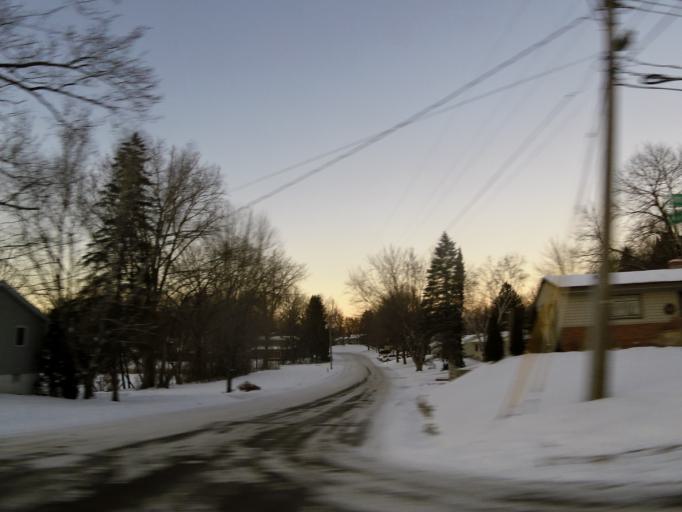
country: US
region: Minnesota
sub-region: Washington County
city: Stillwater
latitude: 45.0549
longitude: -92.8242
